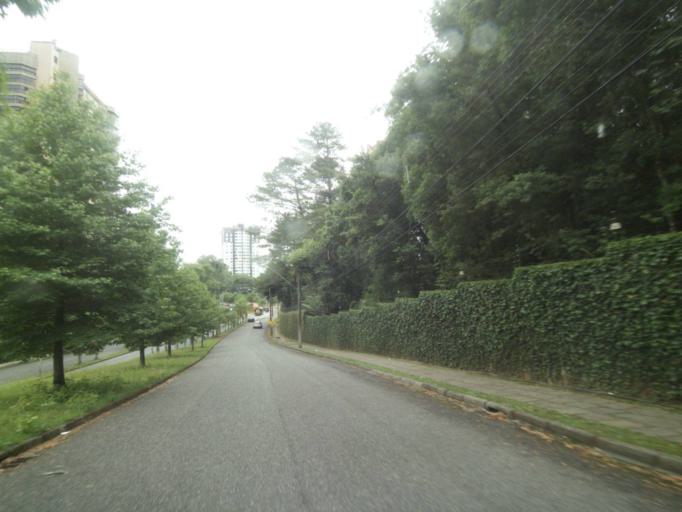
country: BR
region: Parana
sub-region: Curitiba
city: Curitiba
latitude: -25.4367
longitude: -49.3270
